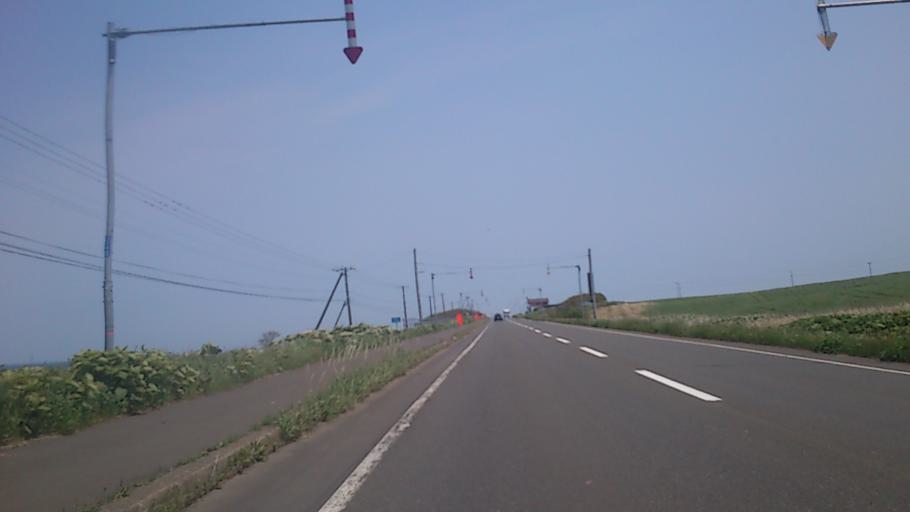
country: JP
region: Hokkaido
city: Nemuro
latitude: 43.2892
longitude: 145.5119
